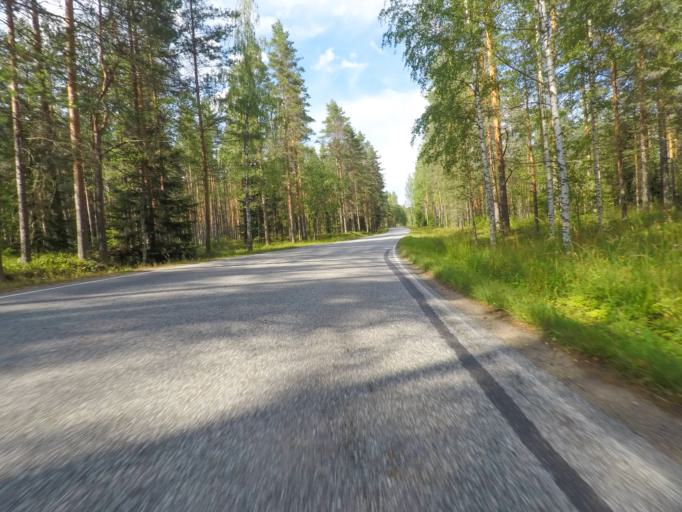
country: FI
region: Southern Savonia
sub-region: Mikkeli
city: Puumala
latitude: 61.7009
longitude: 28.2104
